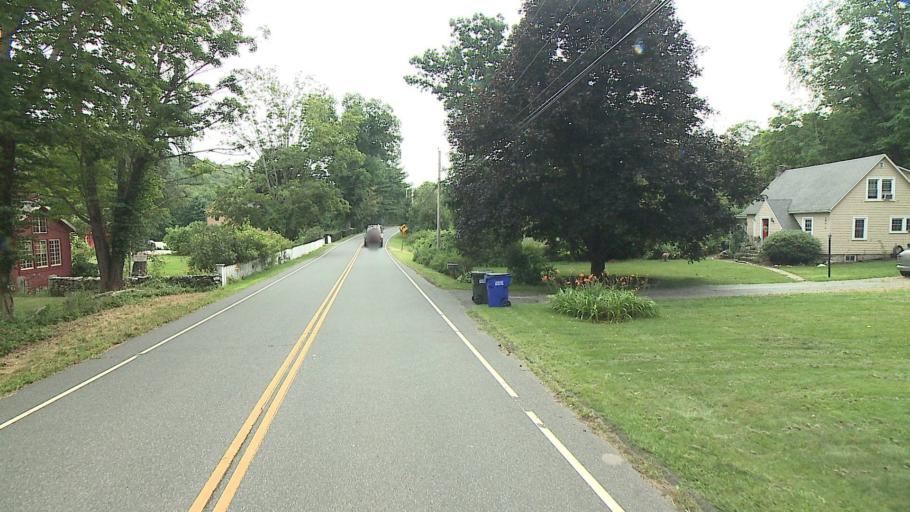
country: US
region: Connecticut
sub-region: Litchfield County
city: Woodbury
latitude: 41.5692
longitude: -73.2236
